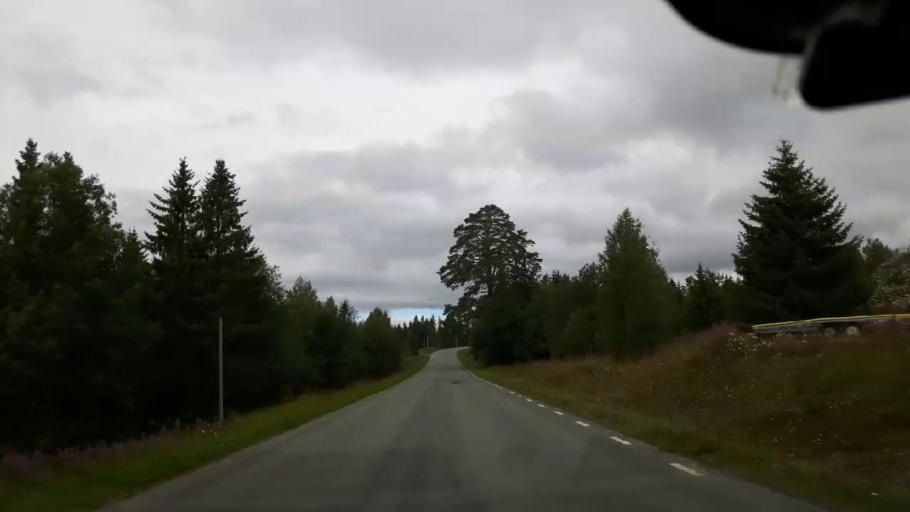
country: SE
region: Jaemtland
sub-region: Krokoms Kommun
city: Valla
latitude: 63.5118
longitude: 13.8837
